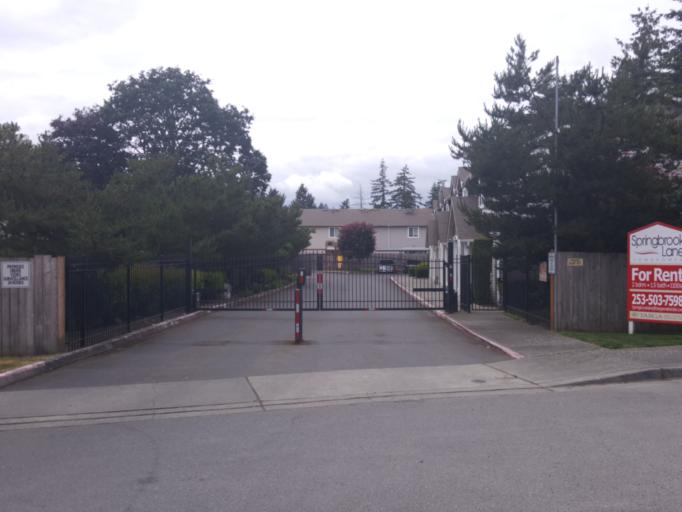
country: US
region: Washington
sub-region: Pierce County
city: McChord Air Force Base
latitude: 47.1443
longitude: -122.5083
